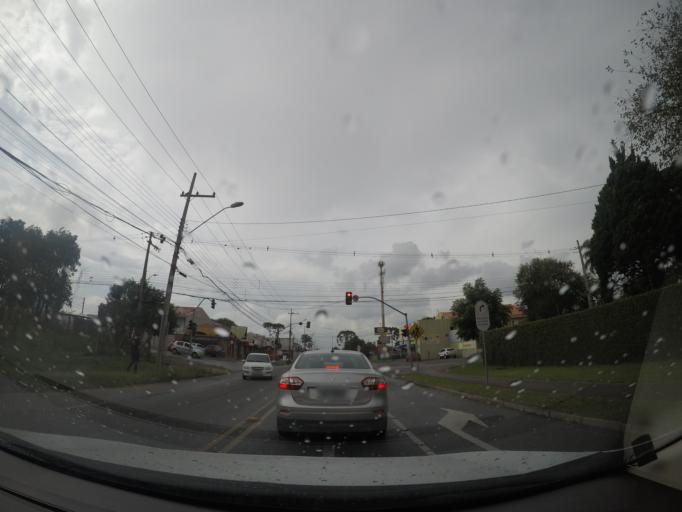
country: BR
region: Parana
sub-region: Sao Jose Dos Pinhais
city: Sao Jose dos Pinhais
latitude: -25.5155
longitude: -49.2460
